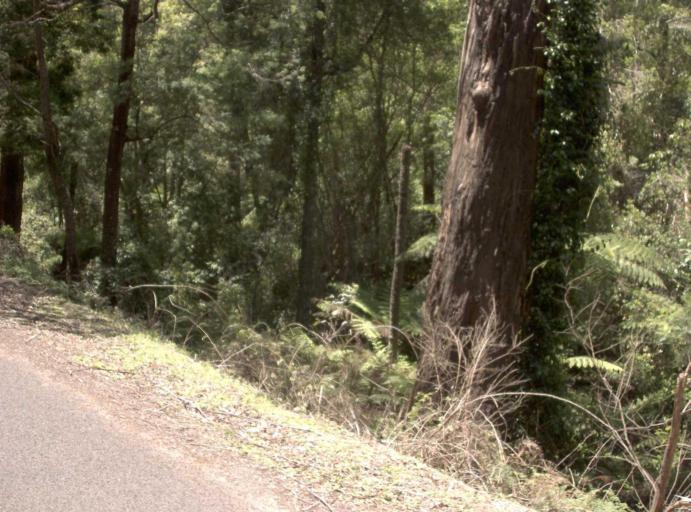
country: AU
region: New South Wales
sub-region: Bombala
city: Bombala
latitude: -37.4593
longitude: 148.9371
